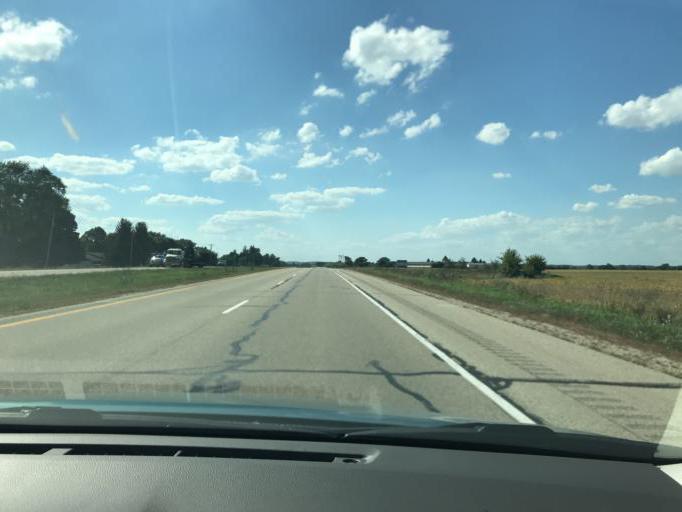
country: US
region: Wisconsin
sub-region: Walworth County
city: Pell Lake
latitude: 42.5968
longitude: -88.3680
